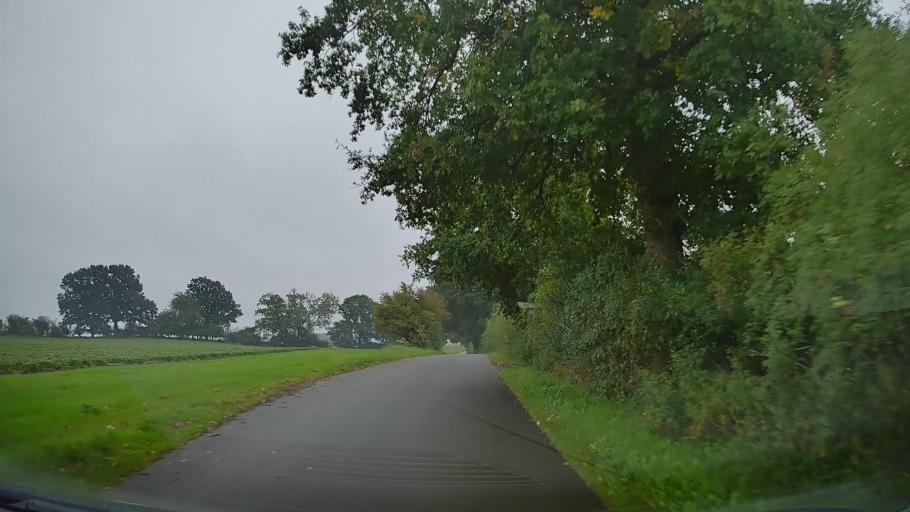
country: DE
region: Mecklenburg-Vorpommern
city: Gramkow
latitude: 53.9245
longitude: 11.3423
